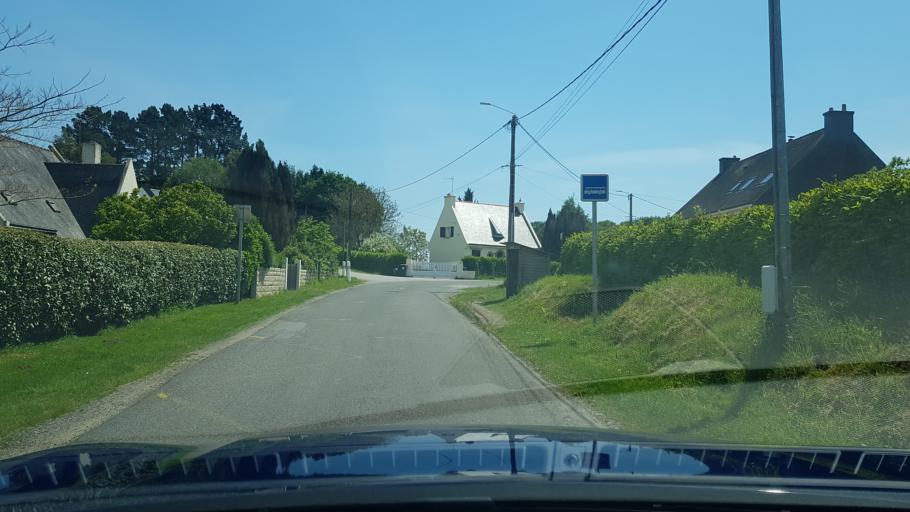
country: FR
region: Brittany
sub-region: Departement du Morbihan
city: Gestel
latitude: 47.8128
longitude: -3.4239
